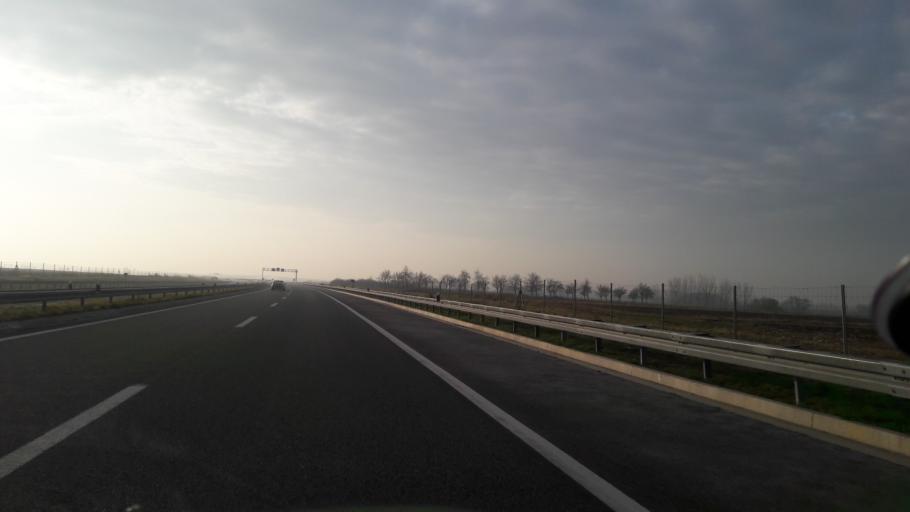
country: HR
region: Osjecko-Baranjska
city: Gorjani
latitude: 45.3706
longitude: 18.3952
